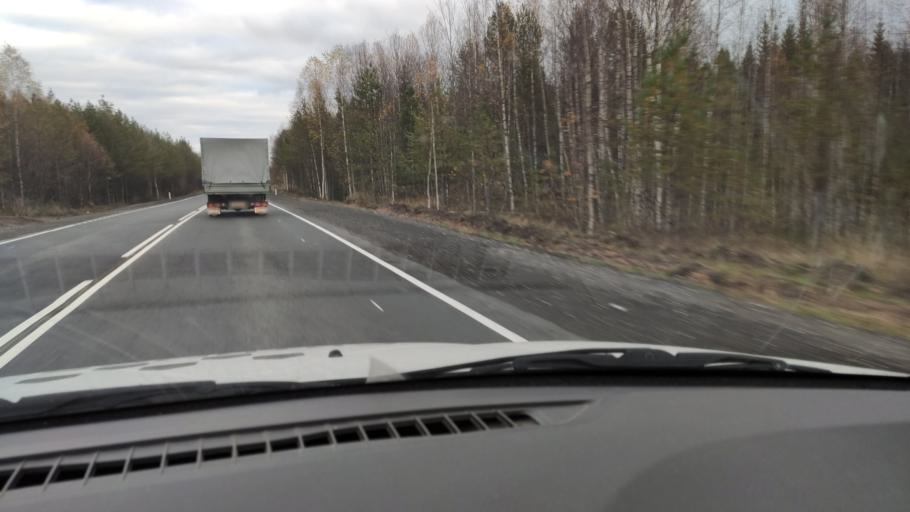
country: RU
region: Kirov
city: Chernaya Kholunitsa
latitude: 58.8737
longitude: 51.5066
